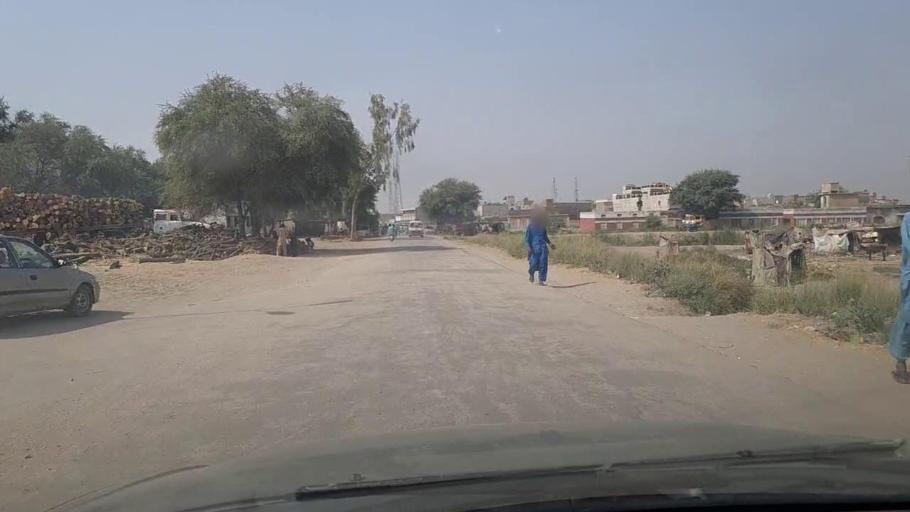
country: PK
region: Sindh
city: Mirpur Mathelo
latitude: 27.9187
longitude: 69.5235
